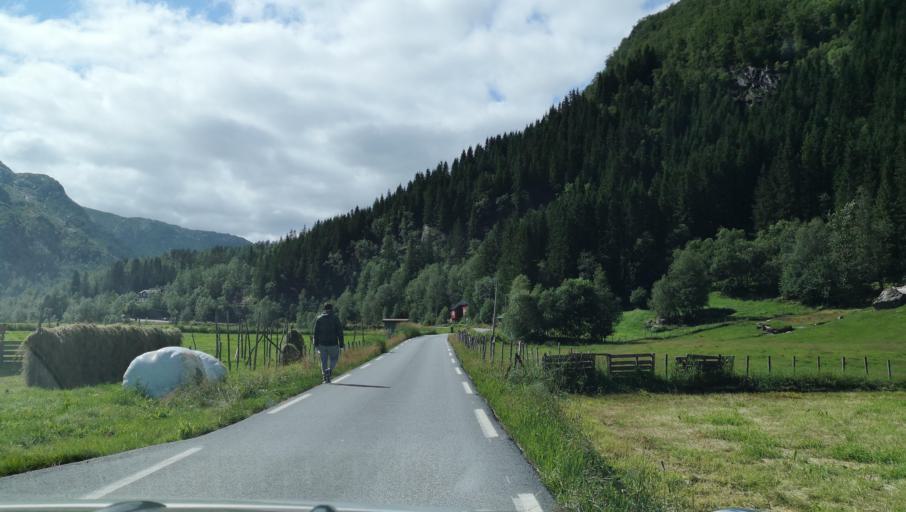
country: NO
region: Hordaland
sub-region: Modalen
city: Mo
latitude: 60.7854
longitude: 5.9605
